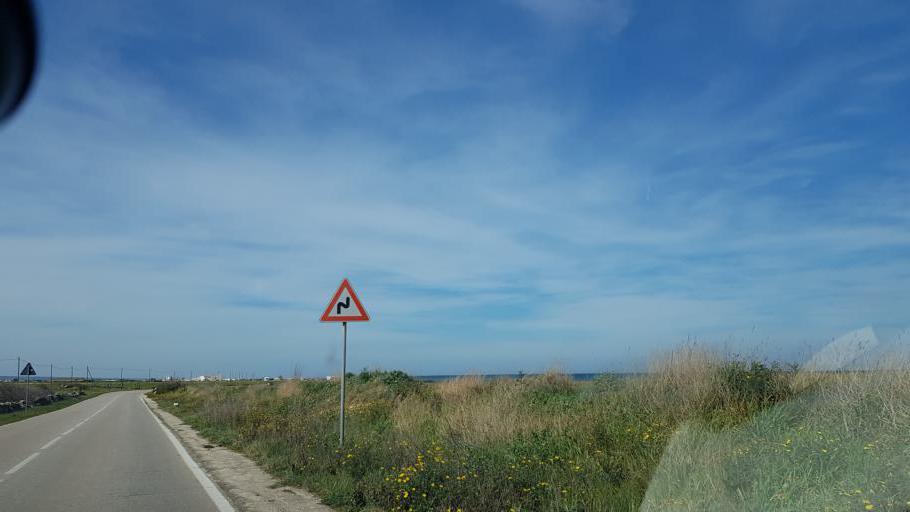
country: IT
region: Apulia
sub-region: Provincia di Brindisi
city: Pezze di Greco
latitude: 40.8481
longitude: 17.4550
